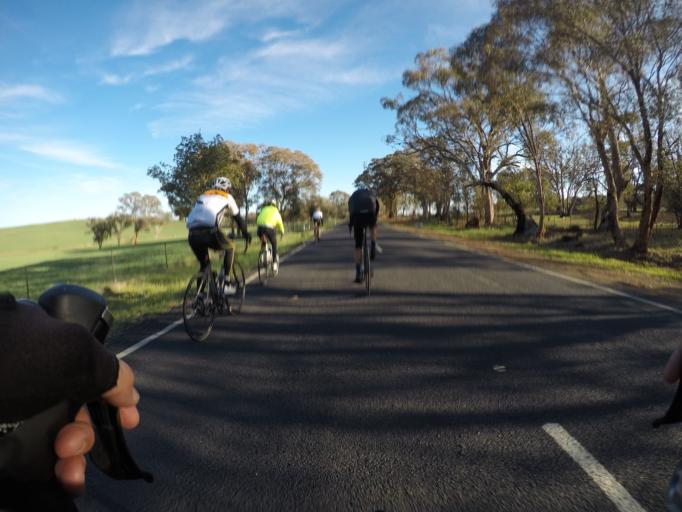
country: AU
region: New South Wales
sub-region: Cabonne
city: Molong
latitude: -32.9532
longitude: 148.7633
